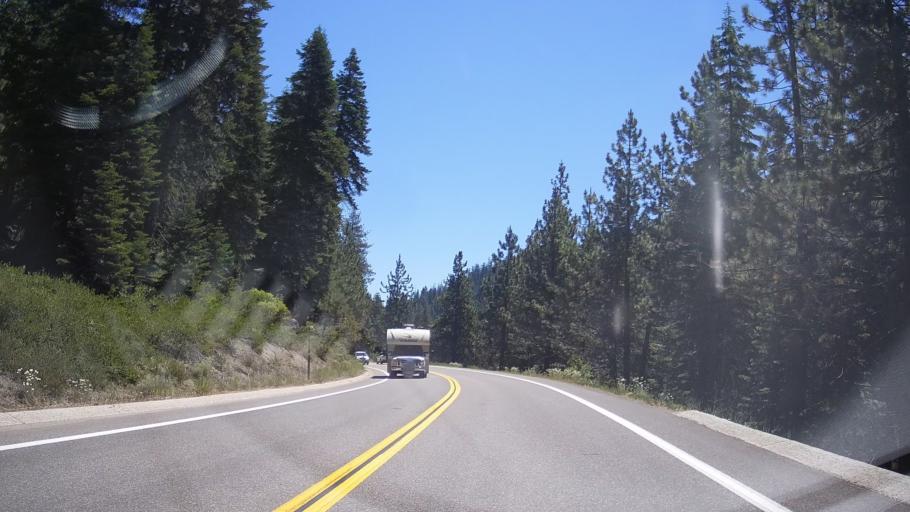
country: US
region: California
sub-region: Placer County
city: Sunnyside-Tahoe City
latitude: 39.1648
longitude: -120.1732
